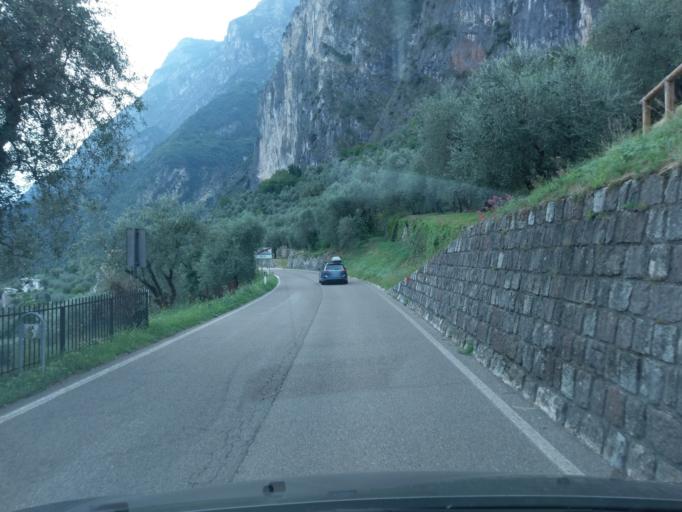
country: IT
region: Trentino-Alto Adige
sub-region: Provincia di Trento
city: Tenno
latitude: 45.9048
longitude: 10.8328
